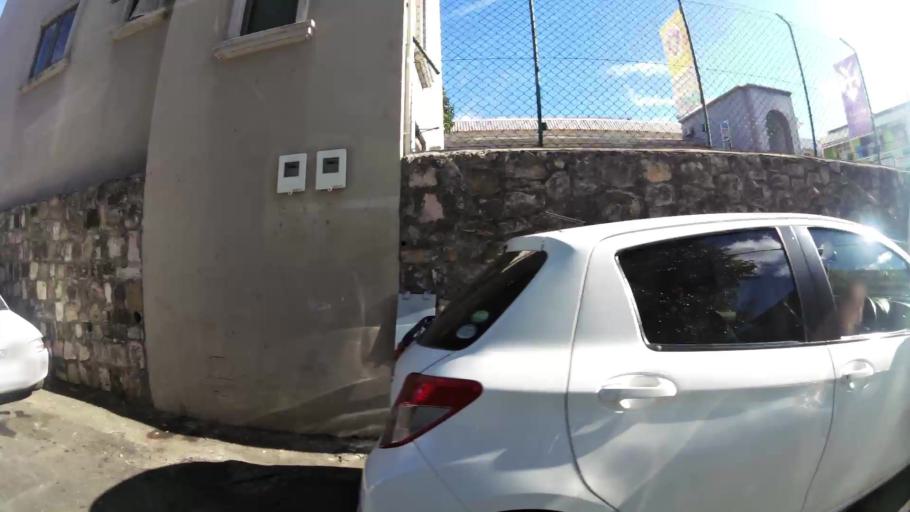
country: MU
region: Port Louis
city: Port Louis
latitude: -20.1574
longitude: 57.5108
